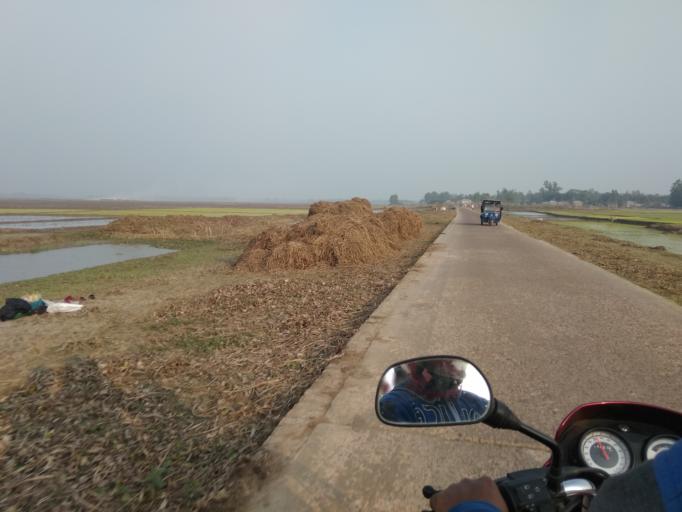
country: BD
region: Rajshahi
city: Ishurdi
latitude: 24.4820
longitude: 89.2276
